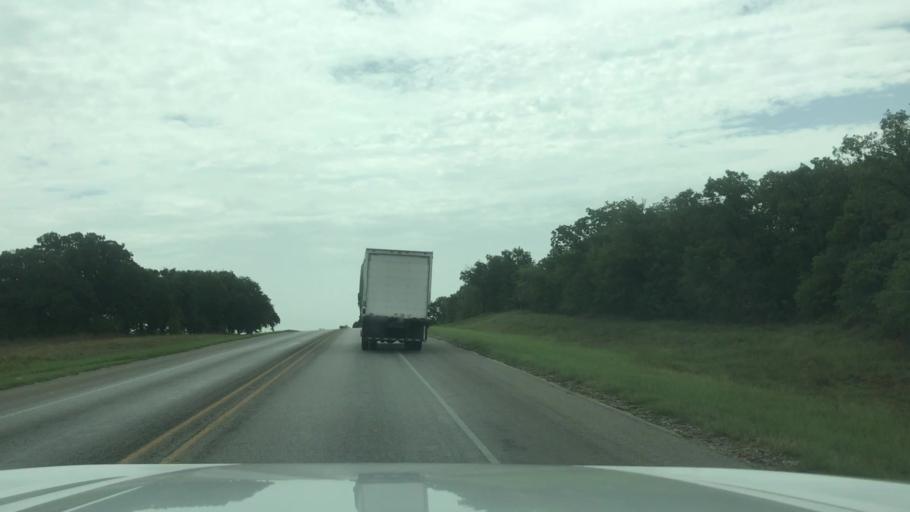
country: US
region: Texas
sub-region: Comanche County
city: De Leon
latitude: 32.1066
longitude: -98.4907
